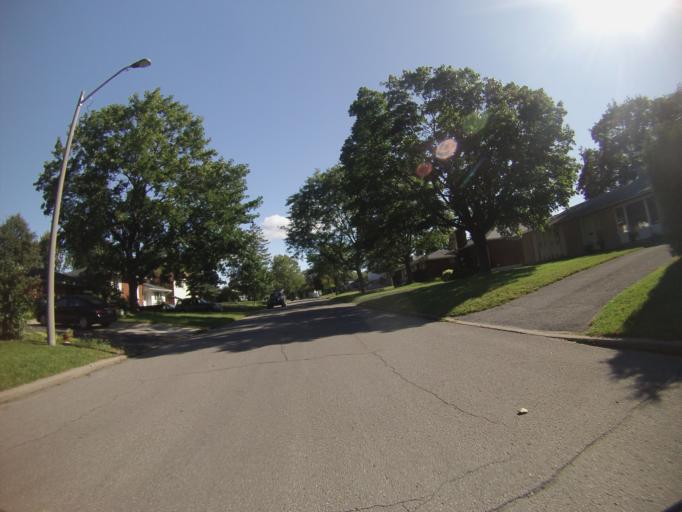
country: CA
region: Ontario
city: Bells Corners
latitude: 45.3468
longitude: -75.7849
